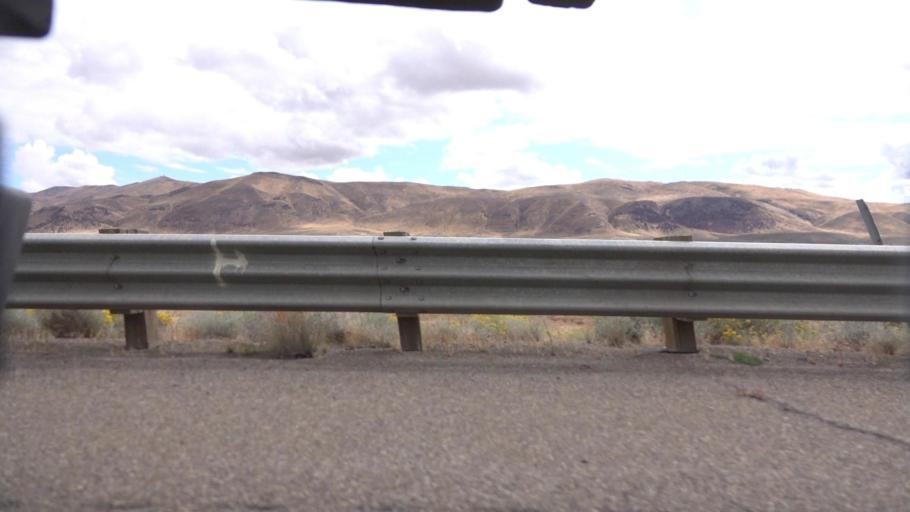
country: US
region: Nevada
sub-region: Elko County
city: Elko
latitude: 40.8922
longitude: -115.7118
